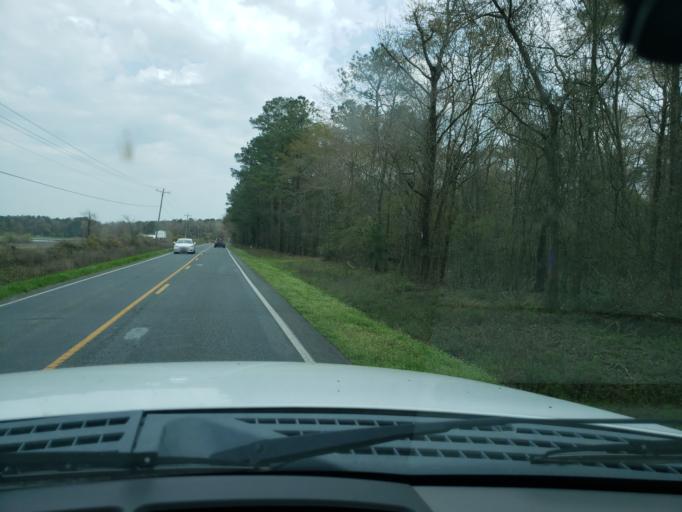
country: US
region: North Carolina
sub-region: Duplin County
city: Beulaville
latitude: 34.7894
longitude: -77.8493
